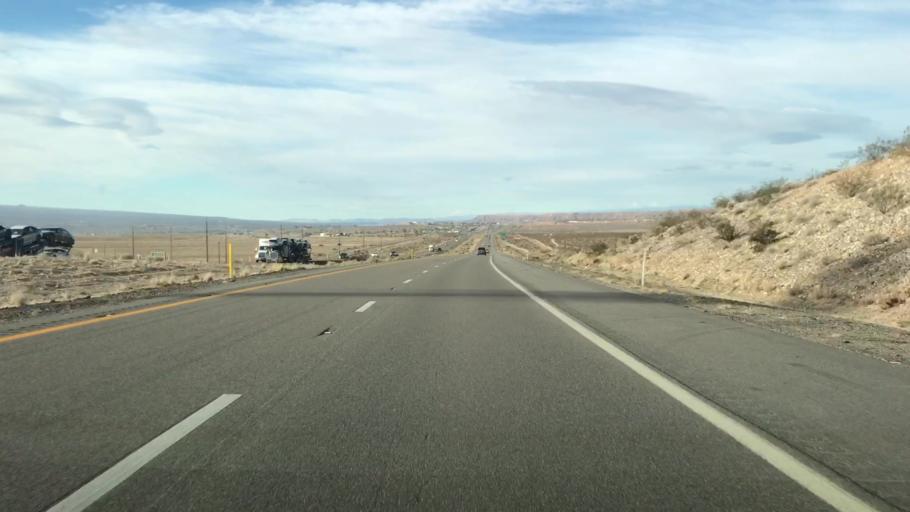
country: US
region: Nevada
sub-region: Clark County
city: Mesquite
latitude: 36.8291
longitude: -114.0138
